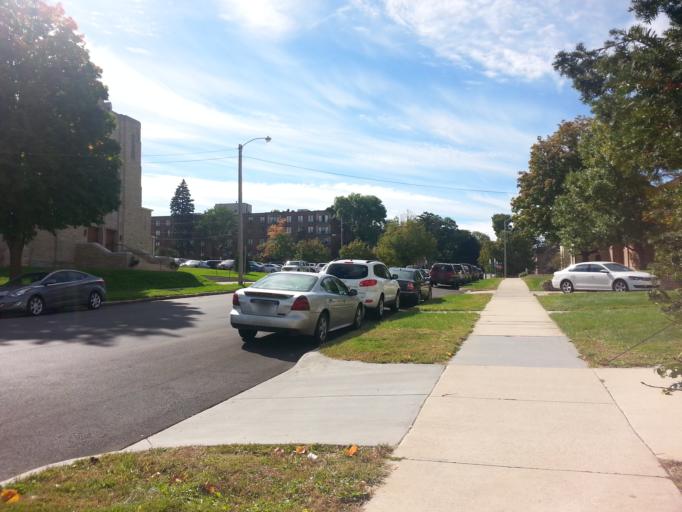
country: US
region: Minnesota
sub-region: Olmsted County
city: Rochester
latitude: 44.0205
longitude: -92.4700
